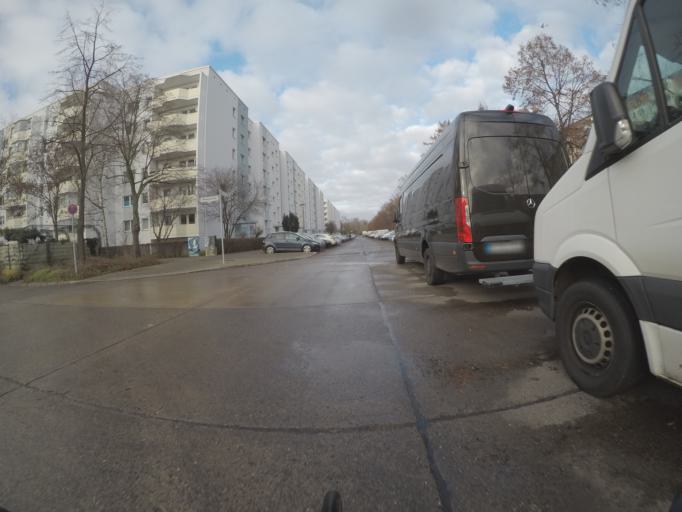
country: DE
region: Berlin
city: Neu-Hohenschoenhausen
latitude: 52.5707
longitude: 13.4963
